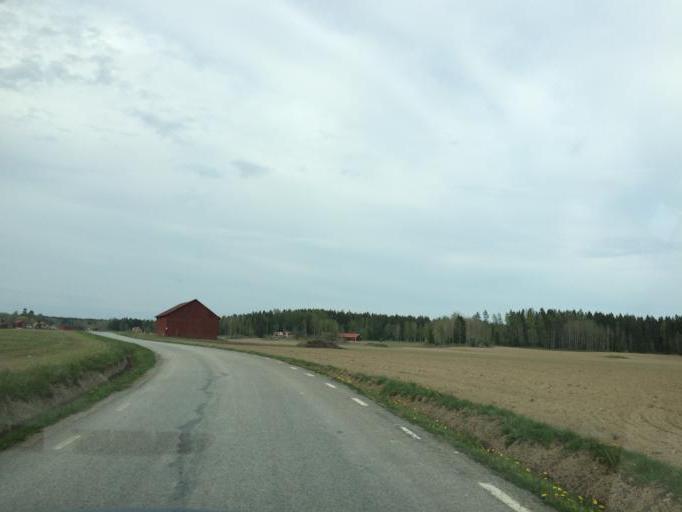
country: SE
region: Vaestmanland
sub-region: Kopings Kommun
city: Koping
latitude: 59.6071
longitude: 16.0224
